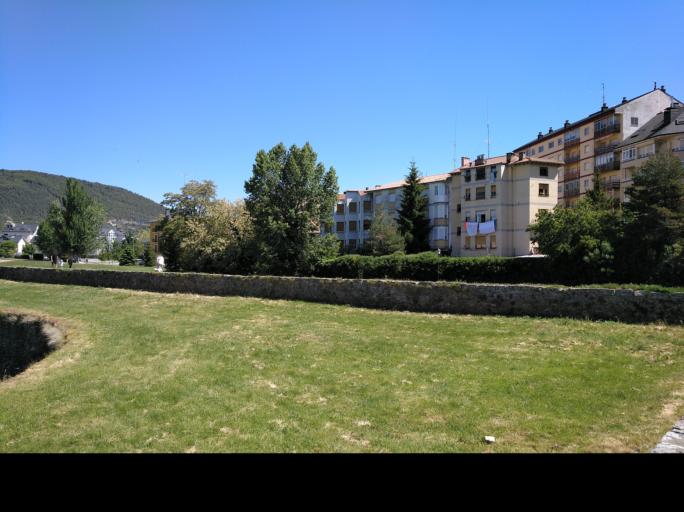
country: ES
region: Aragon
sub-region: Provincia de Huesca
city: Jaca
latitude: 42.5720
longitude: -0.5502
